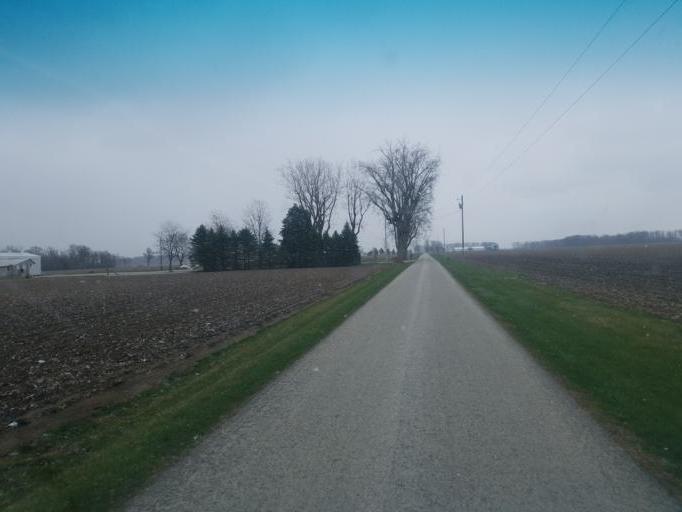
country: US
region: Ohio
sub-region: Marion County
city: Prospect
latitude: 40.4167
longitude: -83.1322
